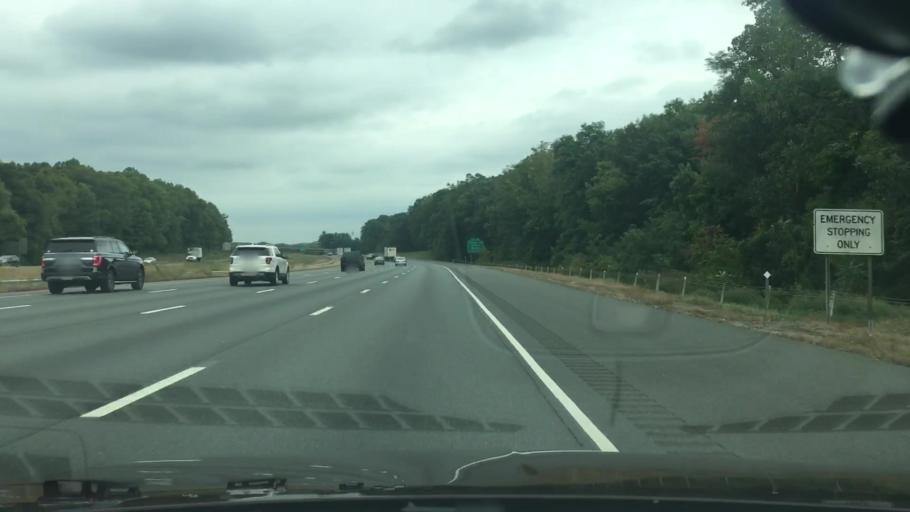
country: US
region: Connecticut
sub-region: Tolland County
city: Rockville
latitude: 41.8293
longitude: -72.4737
